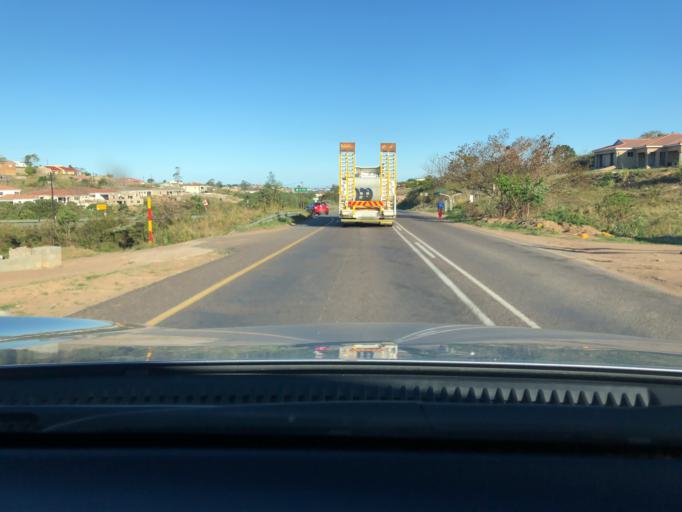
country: ZA
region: KwaZulu-Natal
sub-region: eThekwini Metropolitan Municipality
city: Umkomaas
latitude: -29.9983
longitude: 30.7983
